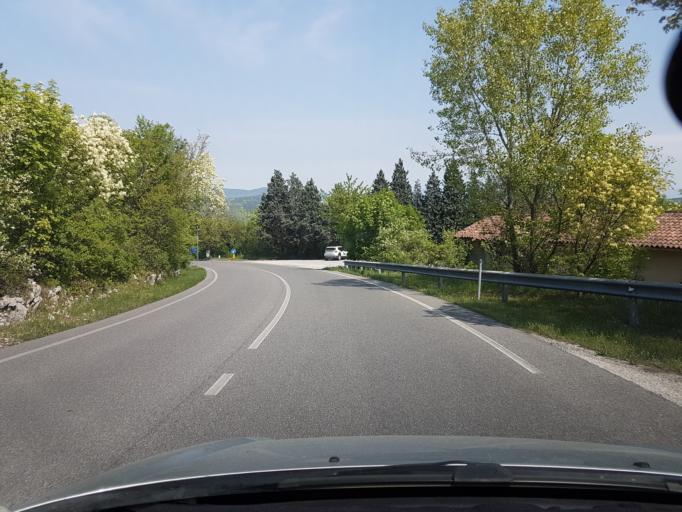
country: IT
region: Friuli Venezia Giulia
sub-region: Provincia di Trieste
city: Aurisina
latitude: 45.7786
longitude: 13.7009
